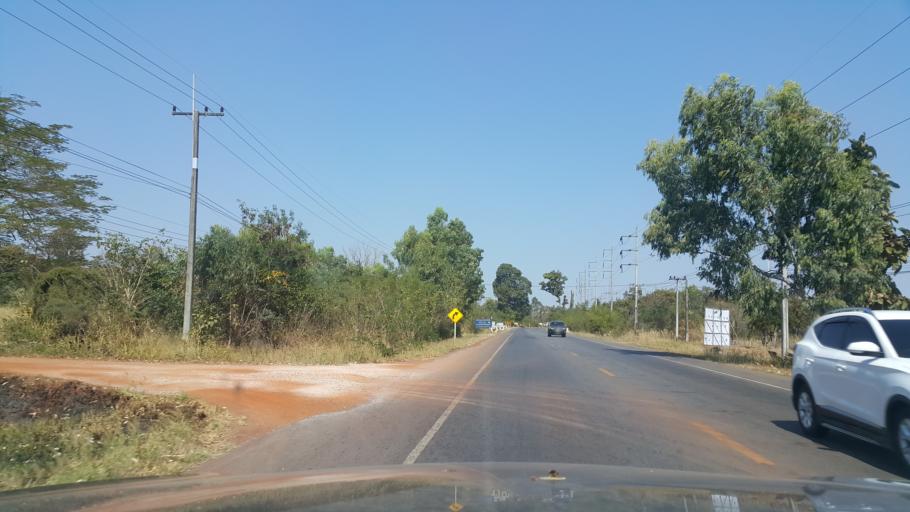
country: TH
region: Changwat Udon Thani
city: Thung Fon
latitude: 17.4382
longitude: 103.1811
